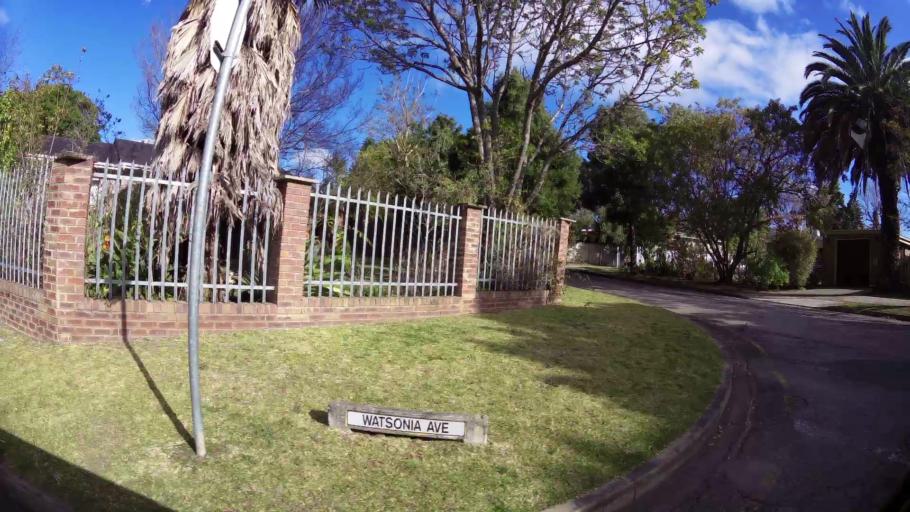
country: ZA
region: Western Cape
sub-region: Eden District Municipality
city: George
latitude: -33.9552
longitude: 22.4776
